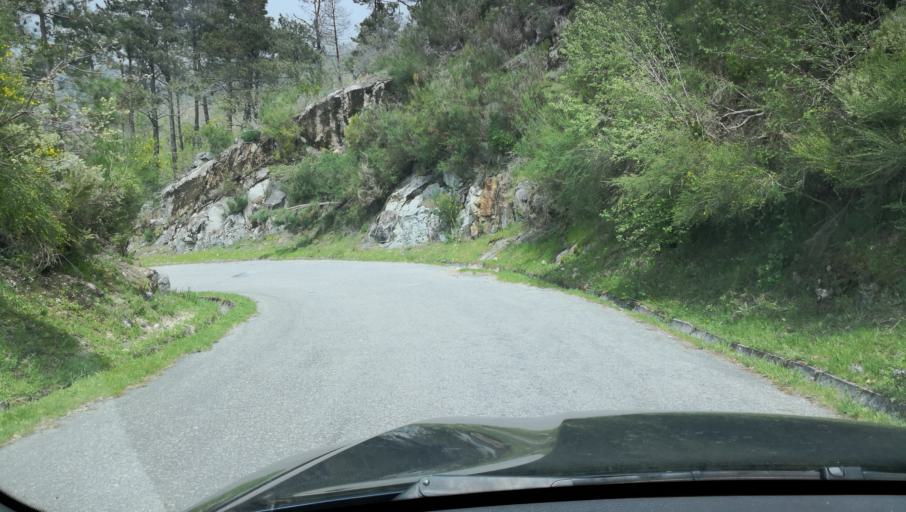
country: PT
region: Vila Real
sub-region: Vila Real
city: Vila Real
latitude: 41.2978
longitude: -7.8329
